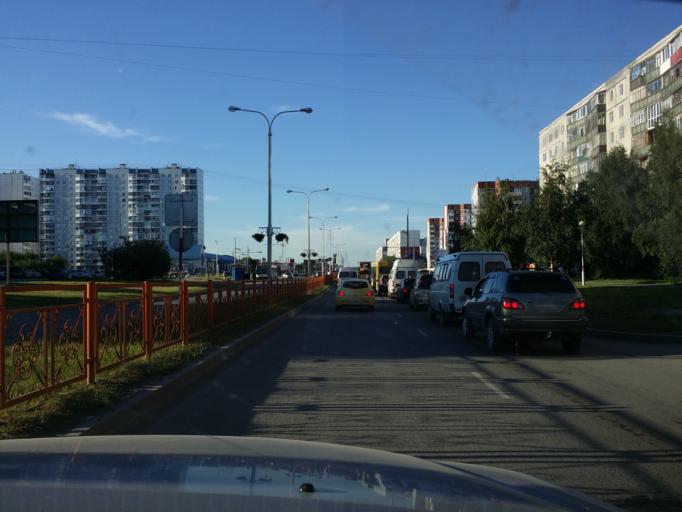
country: RU
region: Khanty-Mansiyskiy Avtonomnyy Okrug
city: Nizhnevartovsk
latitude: 60.9435
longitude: 76.6001
